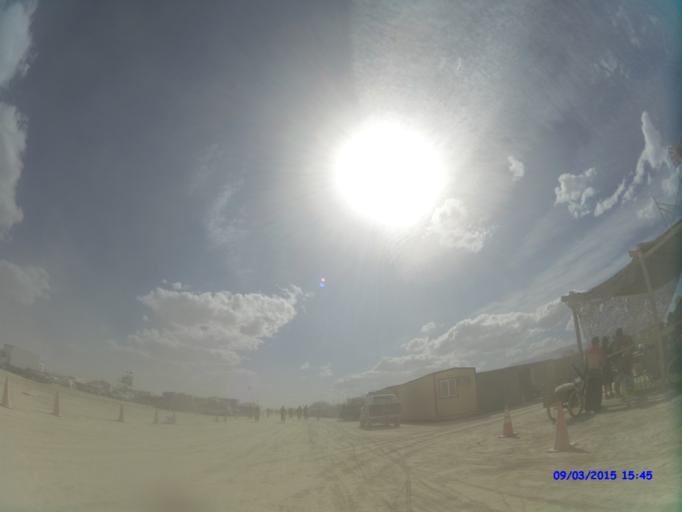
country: US
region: Nevada
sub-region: Pershing County
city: Lovelock
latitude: 40.7929
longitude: -119.2156
